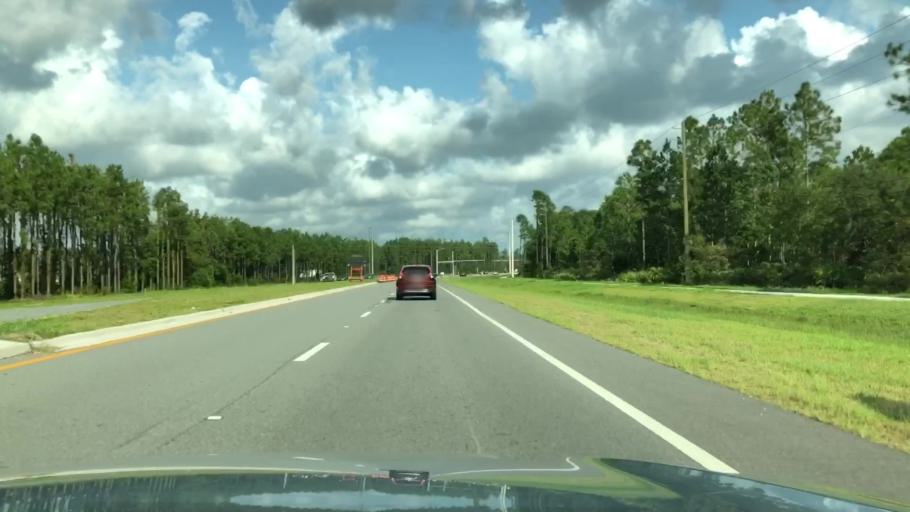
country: US
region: Florida
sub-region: Saint Johns County
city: Fruit Cove
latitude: 30.1047
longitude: -81.5432
